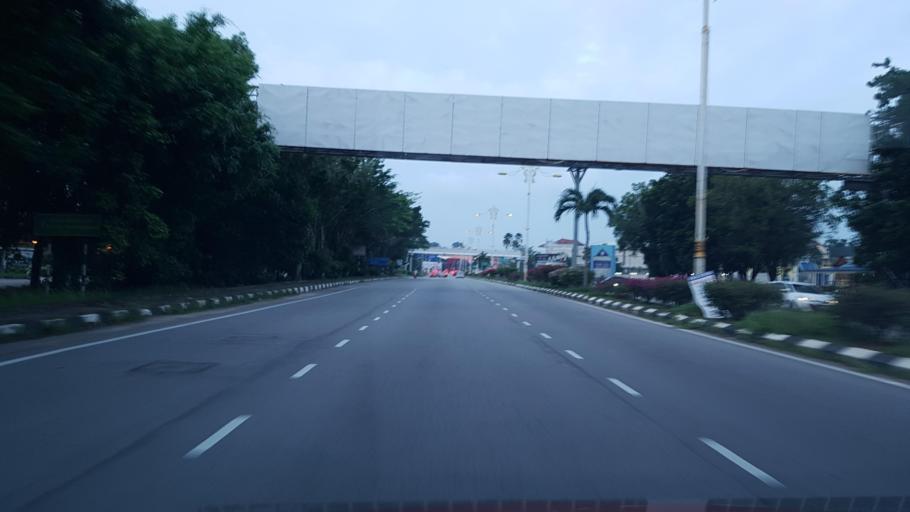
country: MY
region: Terengganu
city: Kuala Terengganu
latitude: 5.3120
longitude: 103.1347
